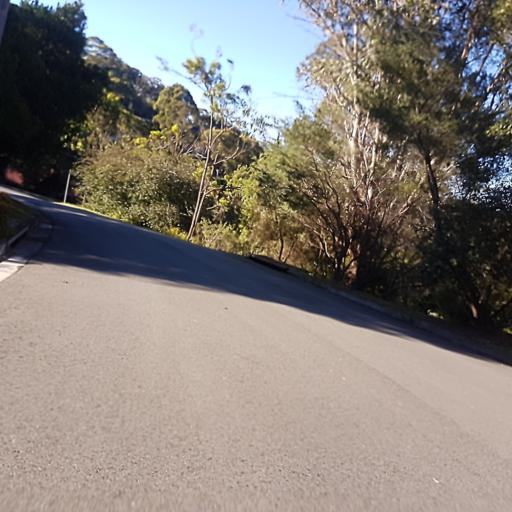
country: AU
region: New South Wales
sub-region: Ku-ring-gai
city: Roseville Chase
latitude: -33.7777
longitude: 151.2043
